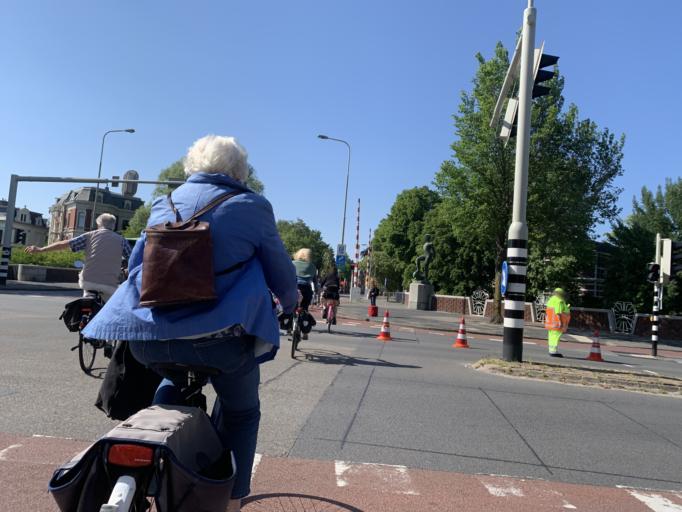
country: NL
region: Groningen
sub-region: Gemeente Groningen
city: Groningen
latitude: 53.2122
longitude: 6.5707
